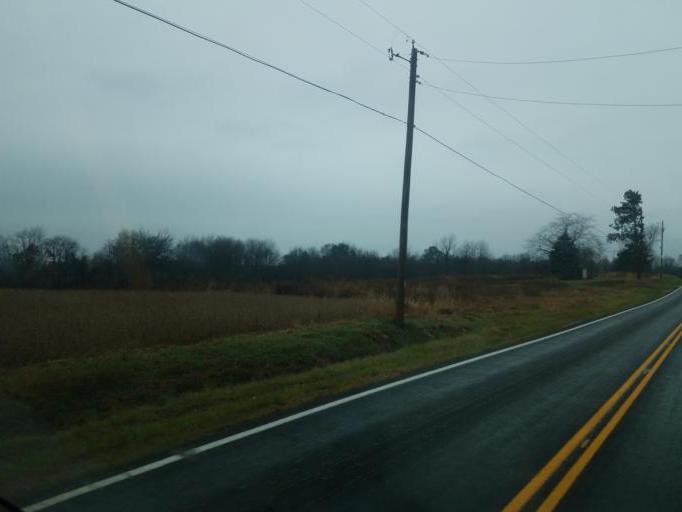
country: US
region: Ohio
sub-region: Sandusky County
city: Bellville
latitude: 40.5599
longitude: -82.5634
